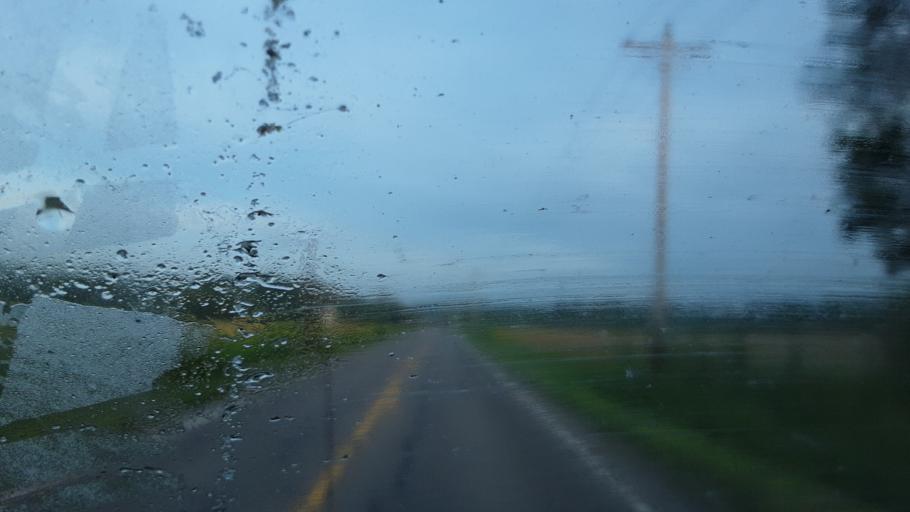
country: US
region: Ohio
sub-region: Ross County
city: Kingston
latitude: 39.4975
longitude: -82.7035
